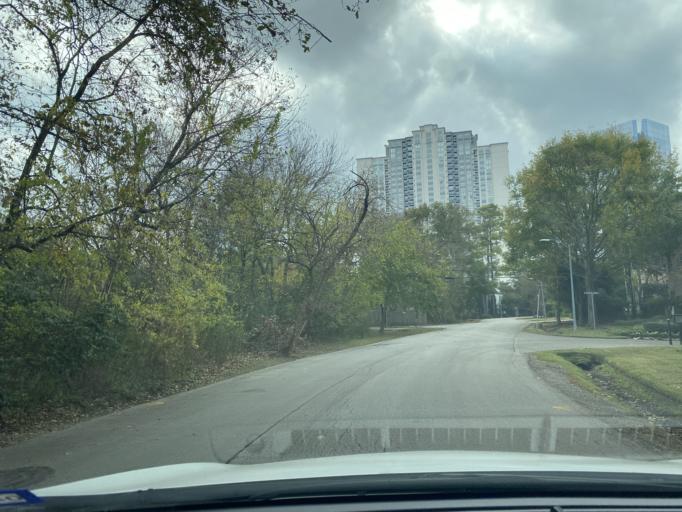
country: US
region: Texas
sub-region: Harris County
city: Hunters Creek Village
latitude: 29.7565
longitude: -95.4596
